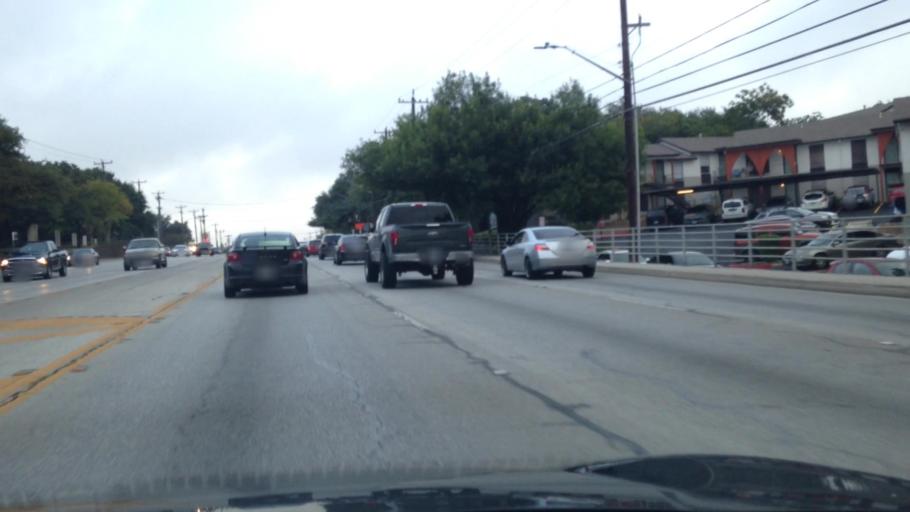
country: US
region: Texas
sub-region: Bexar County
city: Balcones Heights
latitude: 29.5083
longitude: -98.5648
